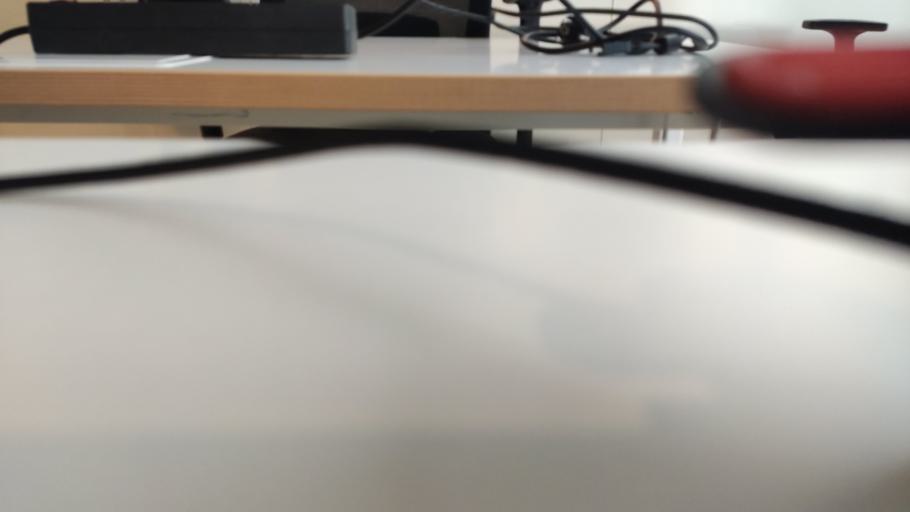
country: RU
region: Moskovskaya
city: Rogachevo
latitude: 56.4113
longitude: 37.0715
